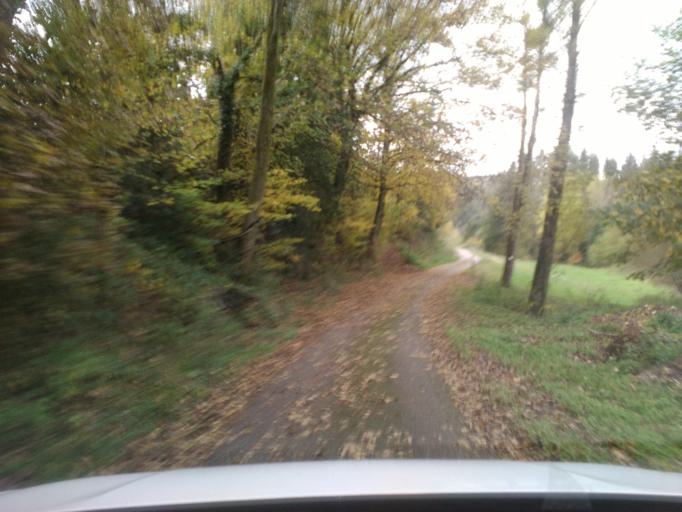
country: FR
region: Lorraine
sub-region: Departement des Vosges
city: Senones
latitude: 48.3747
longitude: 6.9914
